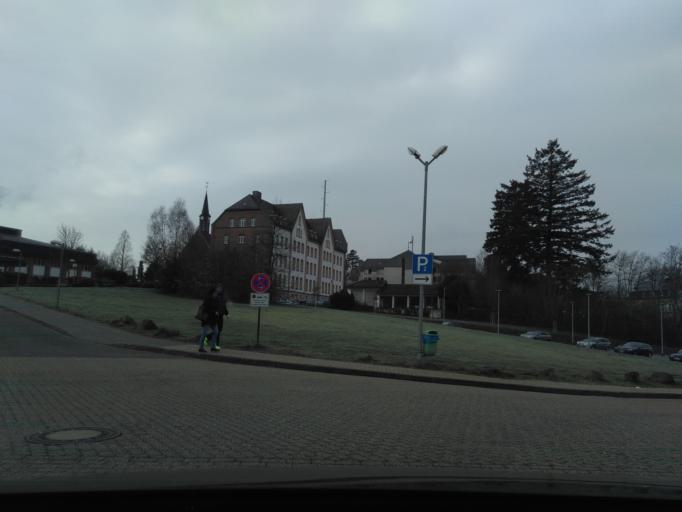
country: DE
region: Rheinland-Pfalz
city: Montabaur
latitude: 50.4323
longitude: 7.8325
